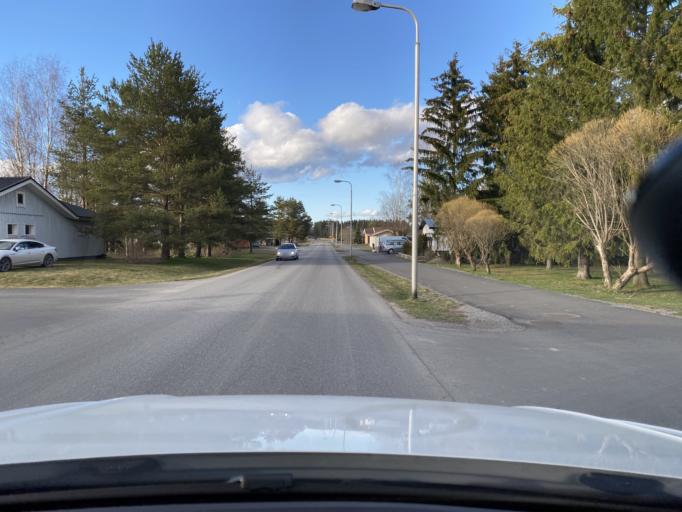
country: FI
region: Pirkanmaa
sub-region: Lounais-Pirkanmaa
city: Punkalaidun
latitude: 61.1155
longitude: 23.1100
